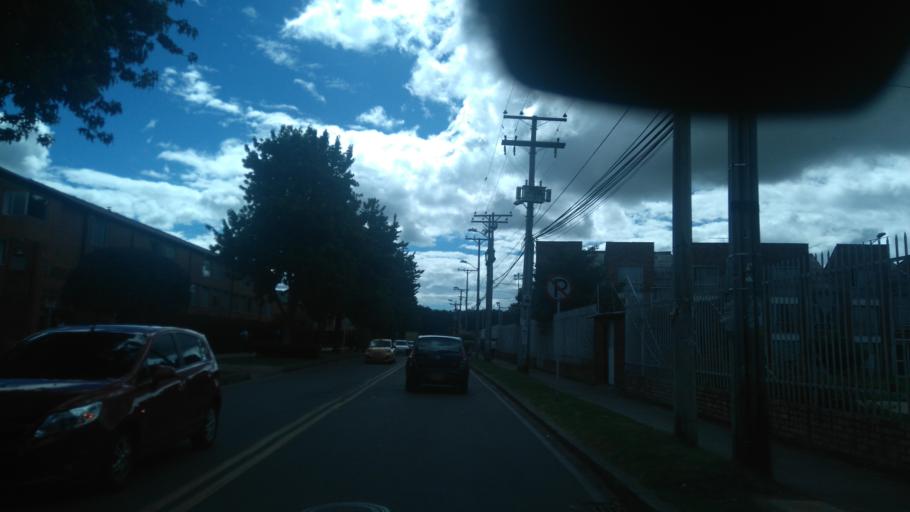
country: CO
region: Cundinamarca
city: Cota
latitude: 4.7604
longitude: -74.0482
